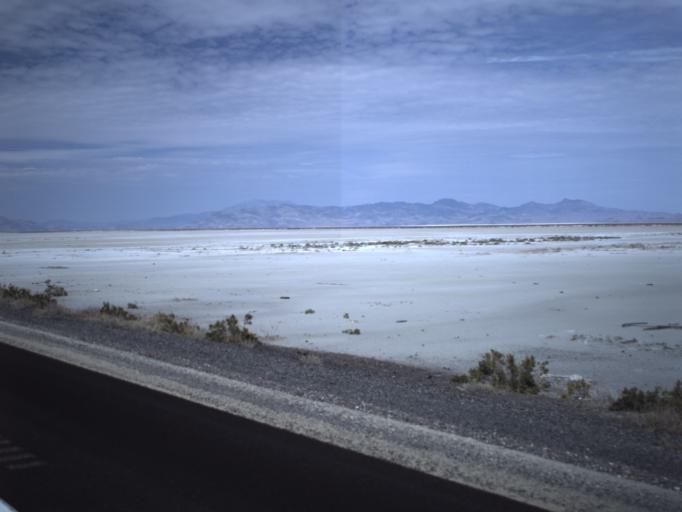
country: US
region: Utah
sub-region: Tooele County
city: Wendover
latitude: 40.7320
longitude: -113.5067
